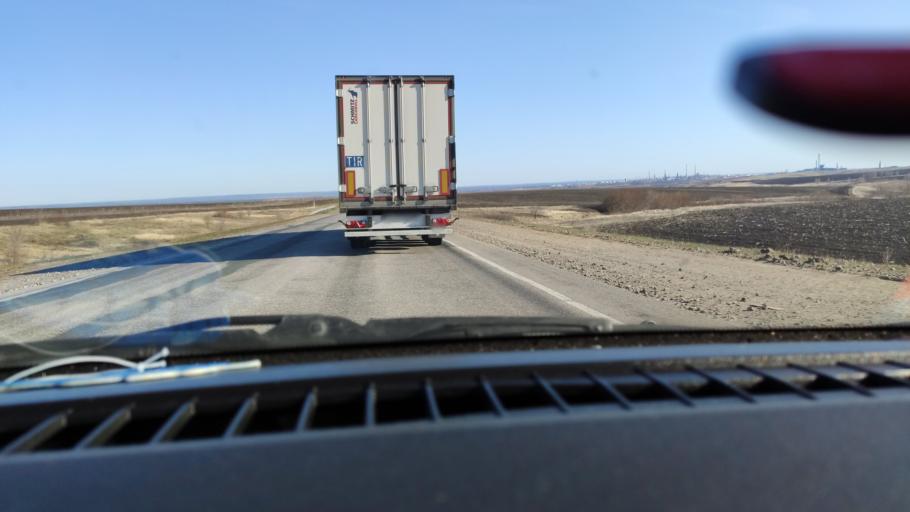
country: RU
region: Samara
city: Varlamovo
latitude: 53.0109
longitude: 48.3324
